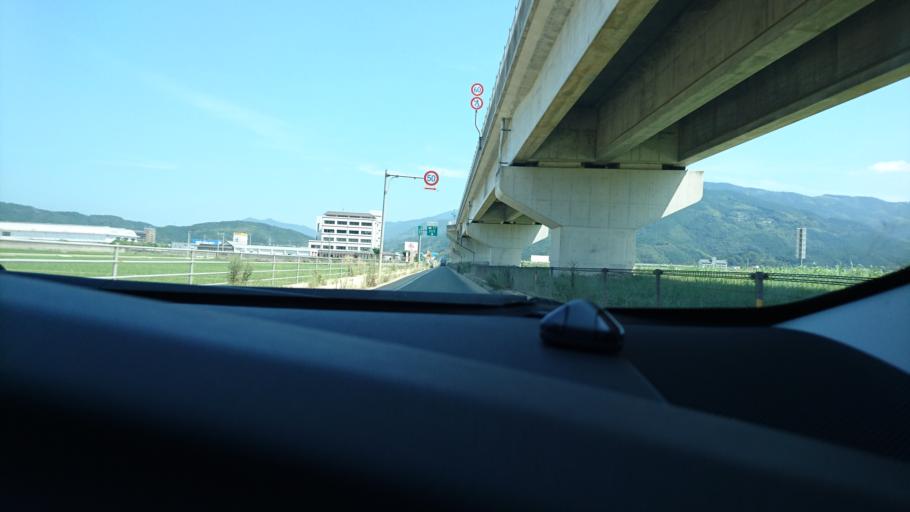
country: JP
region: Ehime
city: Ozu
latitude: 33.5245
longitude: 132.5761
